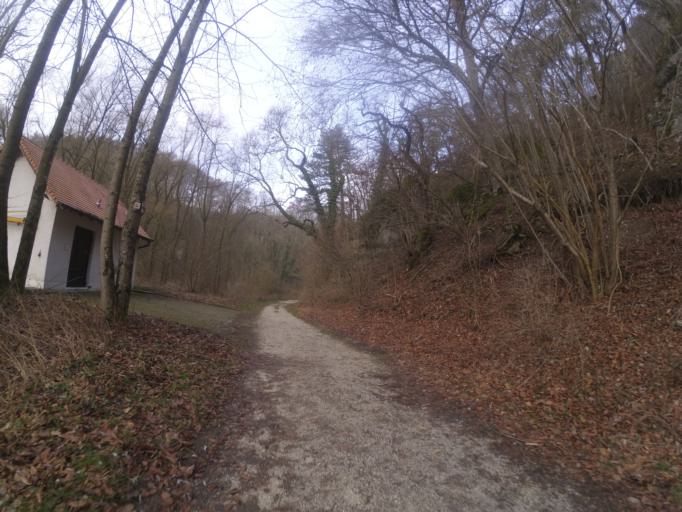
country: DE
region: Baden-Wuerttemberg
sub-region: Tuebingen Region
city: Lauterach
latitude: 48.2456
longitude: 9.5807
